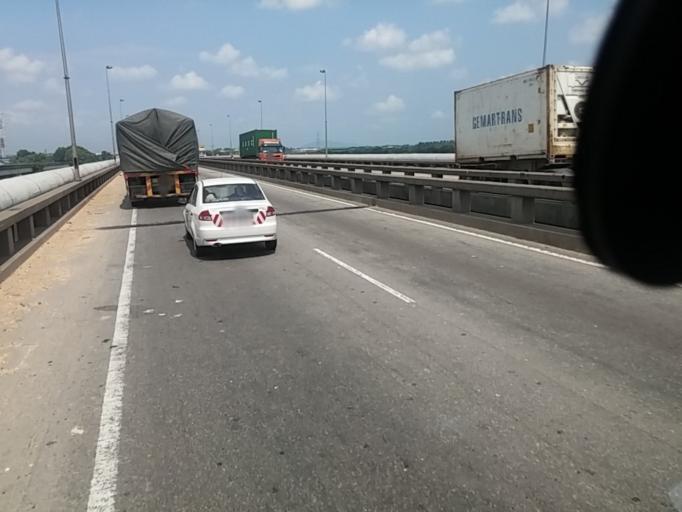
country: MY
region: Selangor
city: Klang
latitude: 2.9836
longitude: 101.3883
